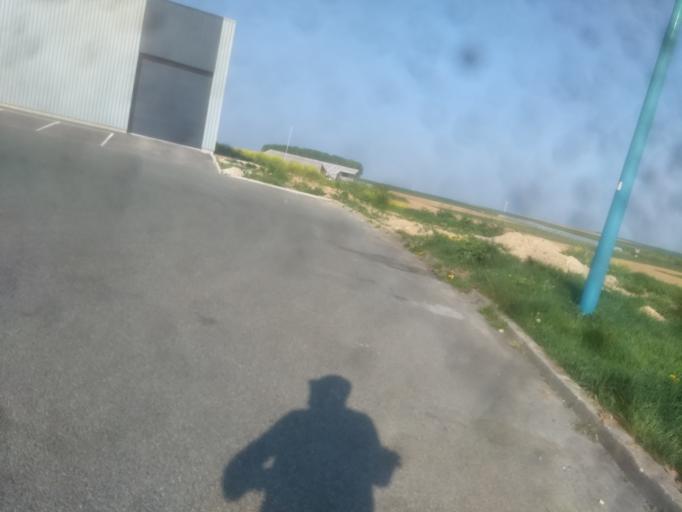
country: FR
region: Nord-Pas-de-Calais
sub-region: Departement du Pas-de-Calais
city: Beaurains
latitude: 50.2627
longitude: 2.7995
